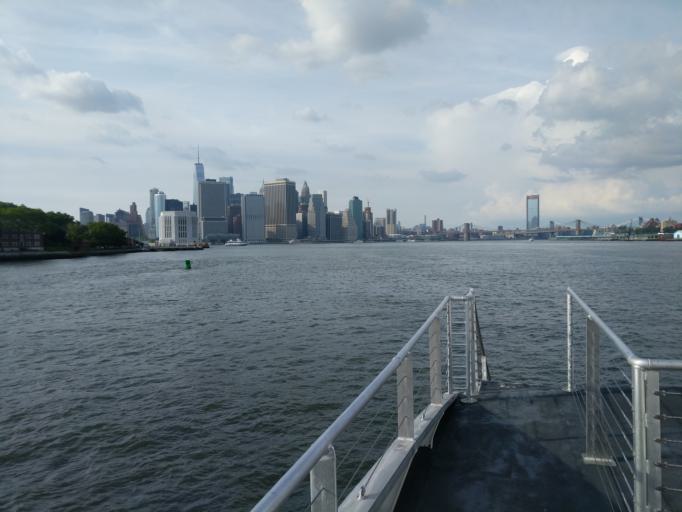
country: US
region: New York
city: New York City
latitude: 40.6871
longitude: -74.0115
